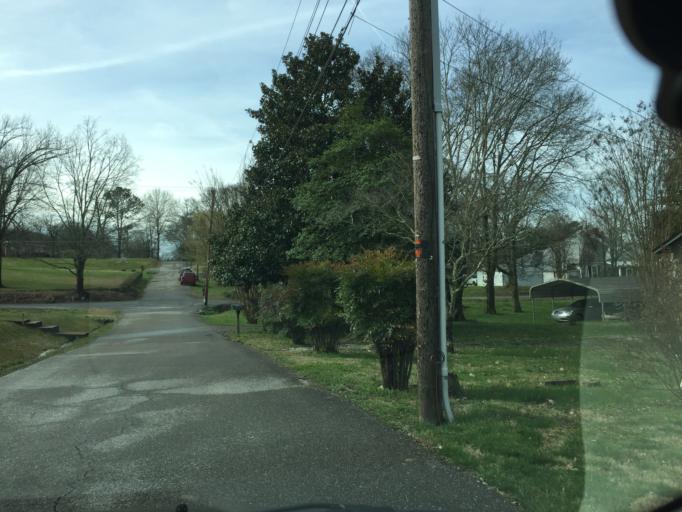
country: US
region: Tennessee
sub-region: Hamilton County
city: Collegedale
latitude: 35.0704
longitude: -85.0577
